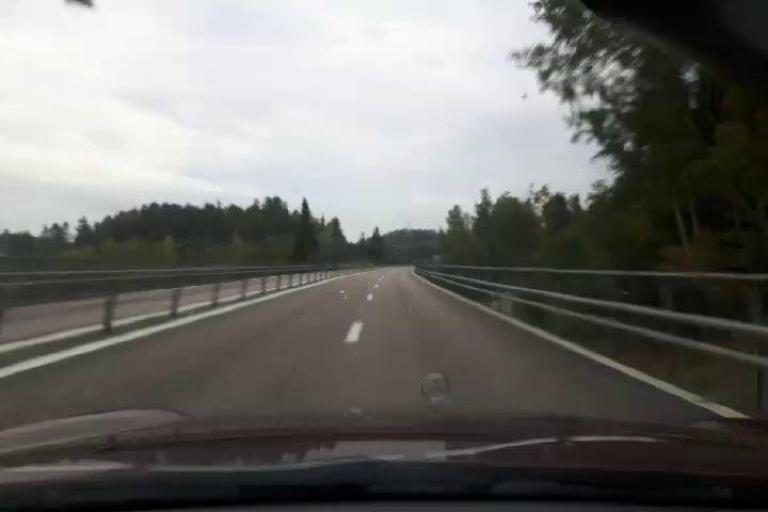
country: SE
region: Vaesternorrland
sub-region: Haernoesands Kommun
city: Haernoesand
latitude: 62.8181
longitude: 17.9690
